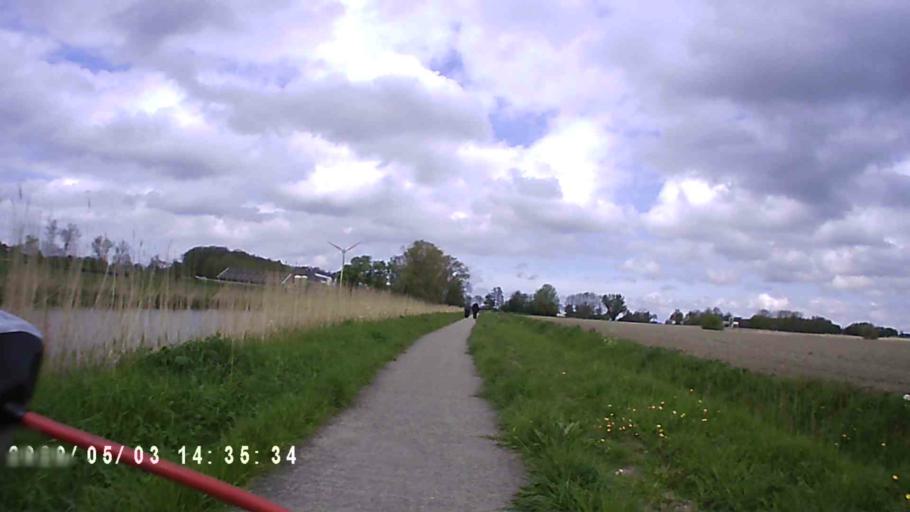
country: NL
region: Groningen
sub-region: Gemeente Zuidhorn
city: Oldehove
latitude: 53.3569
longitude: 6.3943
